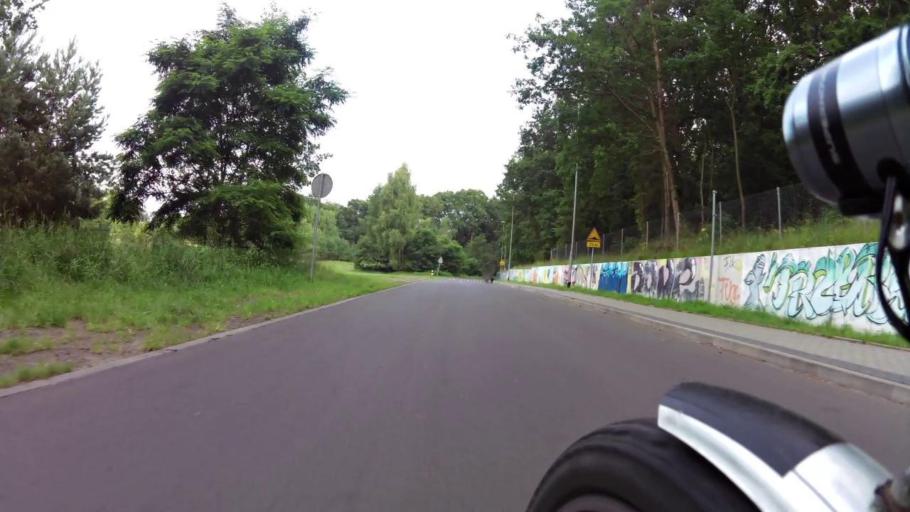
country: PL
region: West Pomeranian Voivodeship
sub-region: Powiat goleniowski
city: Stepnica
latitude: 53.6649
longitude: 14.4948
